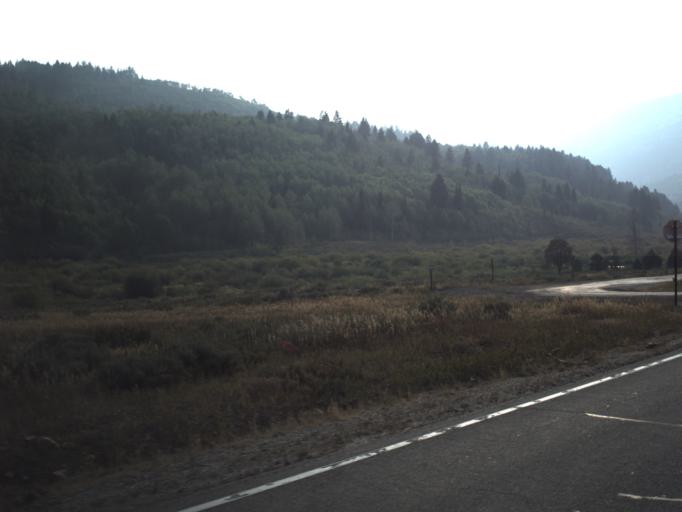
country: US
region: Utah
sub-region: Summit County
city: Kamas
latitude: 40.6305
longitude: -111.1811
